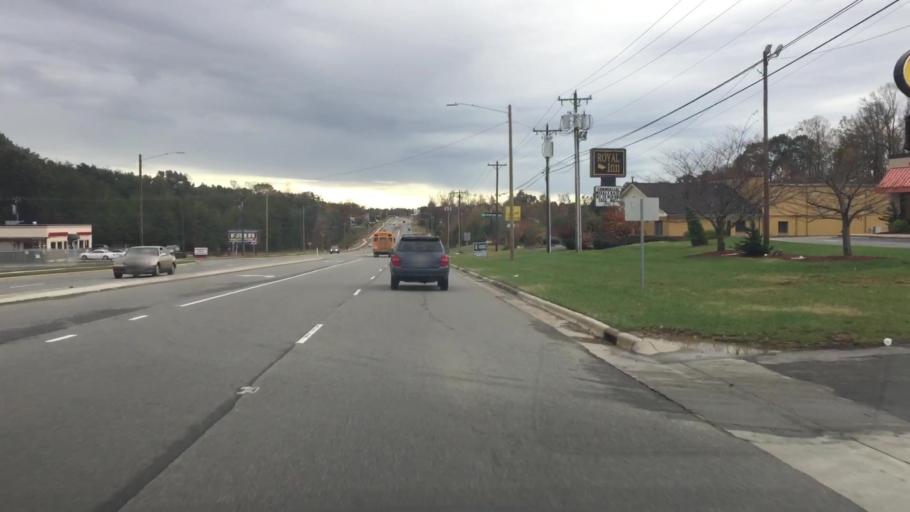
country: US
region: North Carolina
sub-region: Rockingham County
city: Reidsville
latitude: 36.3500
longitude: -79.6930
